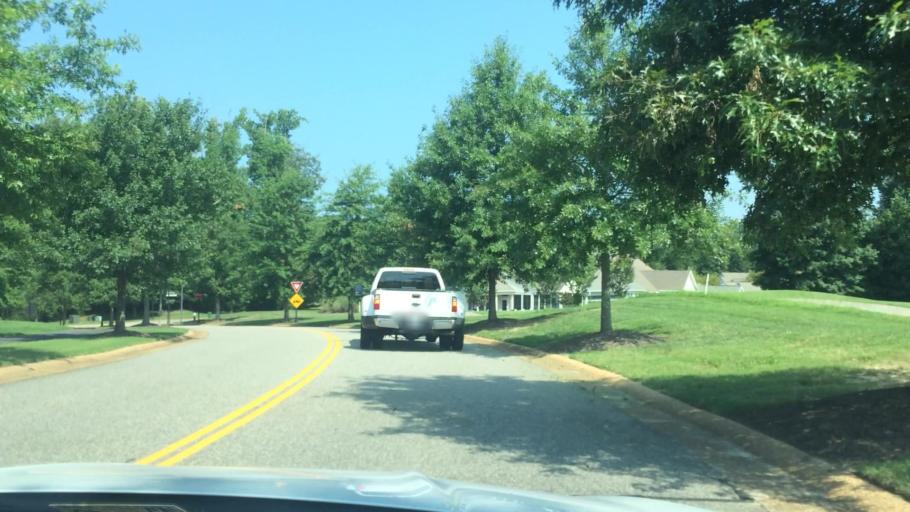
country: US
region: Virginia
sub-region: James City County
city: Williamsburg
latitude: 37.3545
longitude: -76.7706
